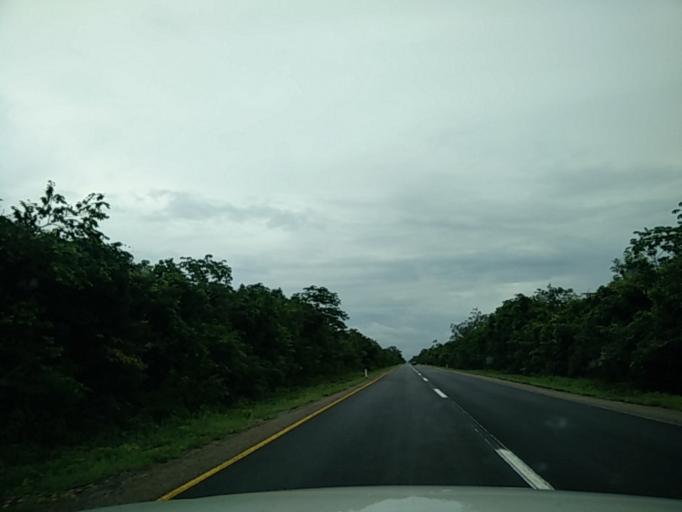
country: MX
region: Quintana Roo
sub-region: Lazaro Cardenas
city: Nuevo Xcan
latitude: 20.8831
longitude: -87.5767
